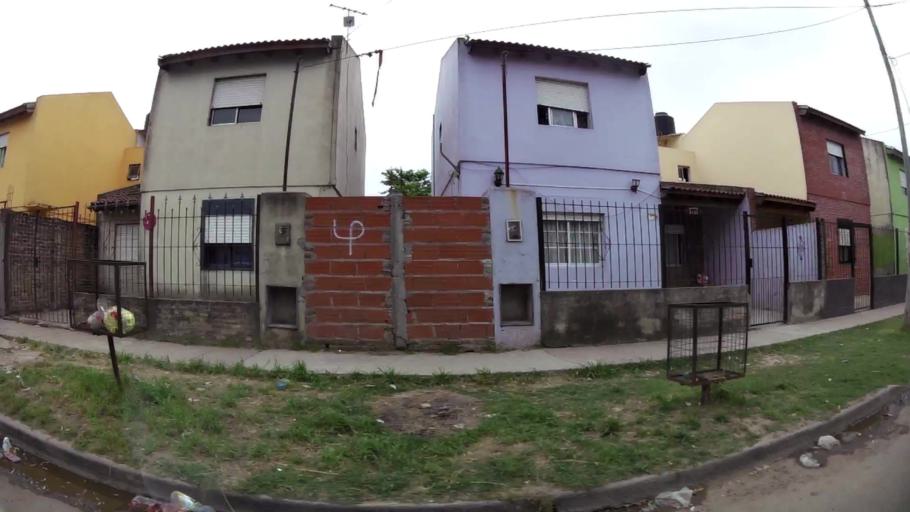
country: AR
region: Buenos Aires
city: San Justo
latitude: -34.6982
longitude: -58.5502
